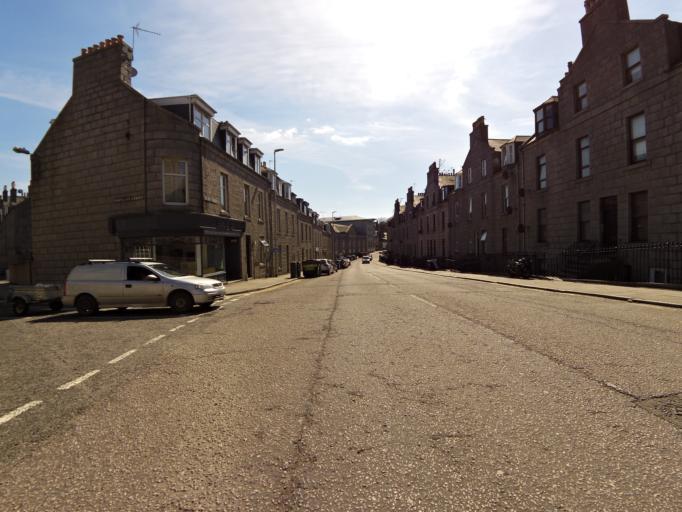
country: GB
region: Scotland
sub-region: Aberdeen City
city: Aberdeen
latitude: 57.1406
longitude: -2.1007
